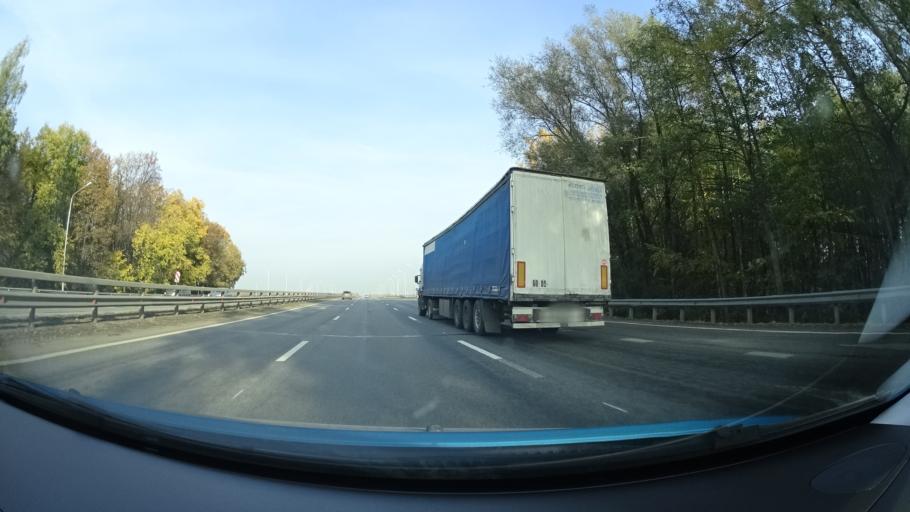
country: RU
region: Bashkortostan
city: Avdon
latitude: 54.6634
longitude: 55.7283
